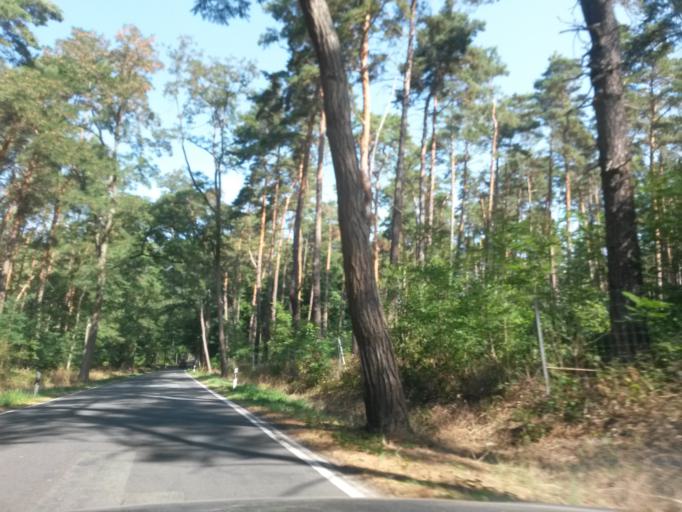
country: DE
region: Brandenburg
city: Wiesenburg
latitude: 52.0151
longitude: 12.3788
